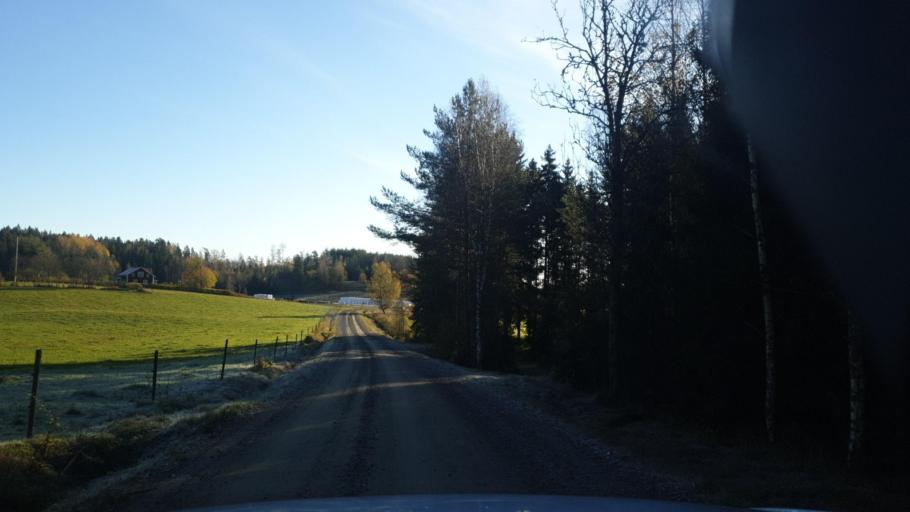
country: SE
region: Vaermland
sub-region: Karlstads Kommun
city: Edsvalla
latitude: 59.5087
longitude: 13.0230
